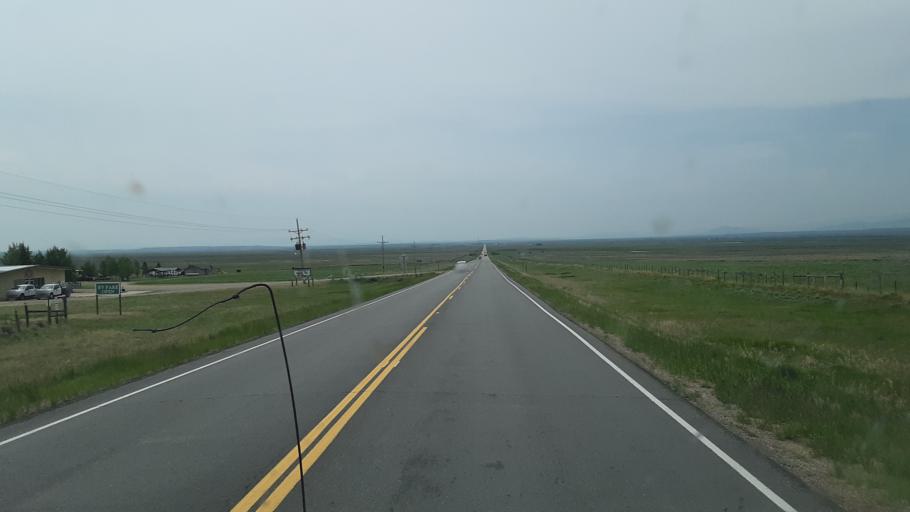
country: US
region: Colorado
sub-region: Jackson County
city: Walden
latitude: 40.9095
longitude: -106.2923
